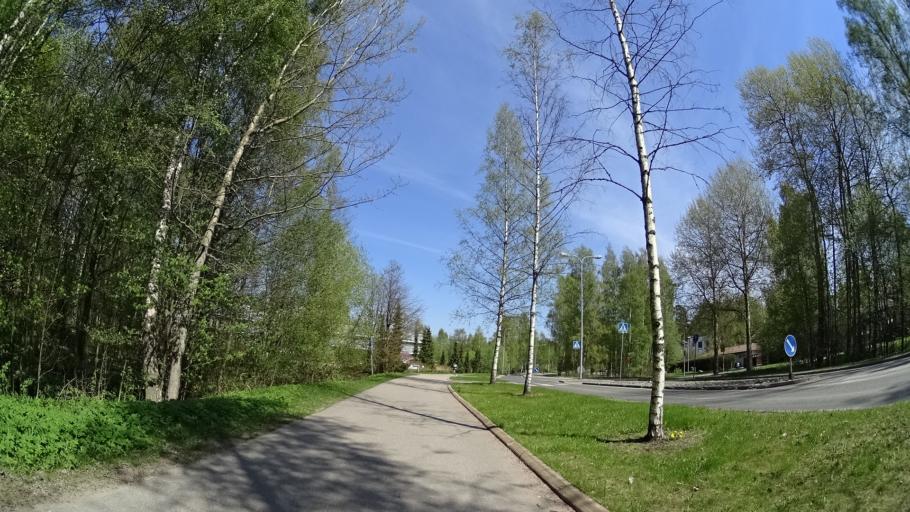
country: FI
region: Uusimaa
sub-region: Helsinki
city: Koukkuniemi
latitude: 60.1668
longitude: 24.7907
